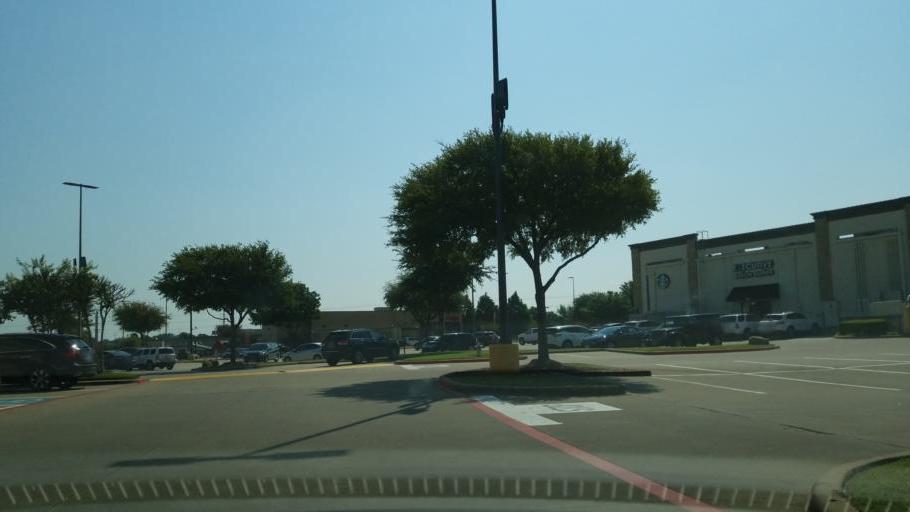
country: US
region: Texas
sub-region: Collin County
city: Allen
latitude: 33.1020
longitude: -96.6842
